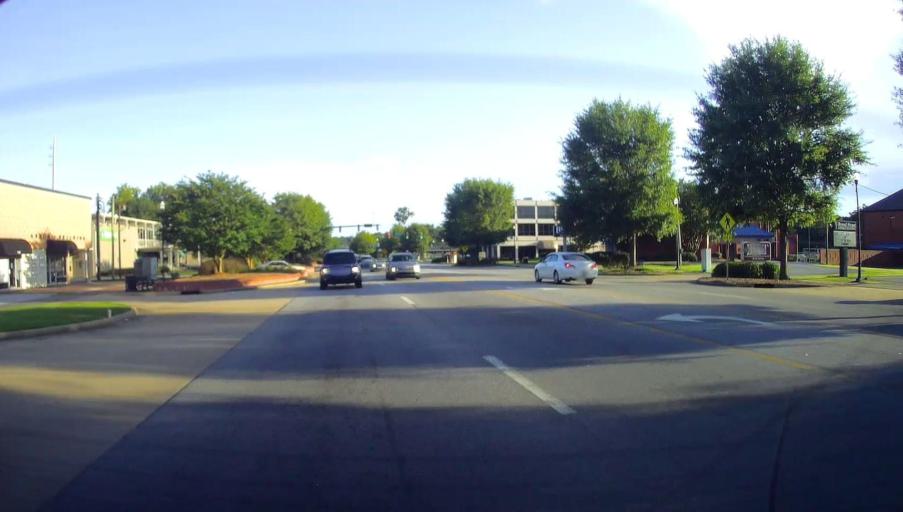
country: US
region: Alabama
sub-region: Russell County
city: Phenix City
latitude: 32.4700
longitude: -85.0008
